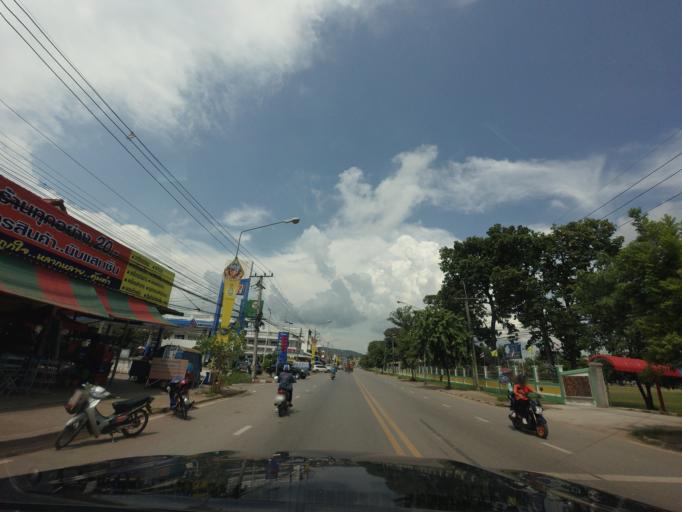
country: TH
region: Khon Kaen
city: Phu Wiang
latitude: 16.6552
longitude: 102.3741
